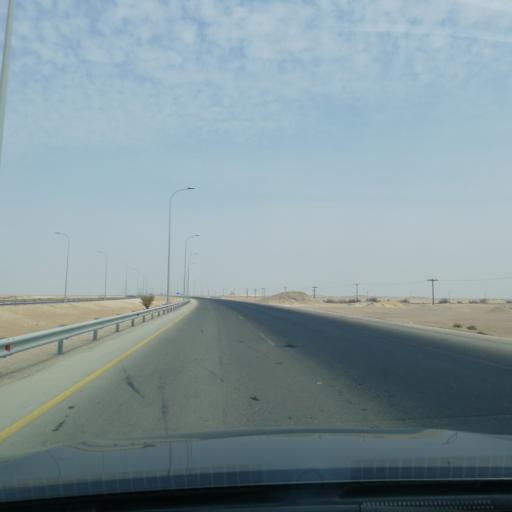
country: OM
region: Zufar
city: Salalah
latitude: 17.6950
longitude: 54.0486
